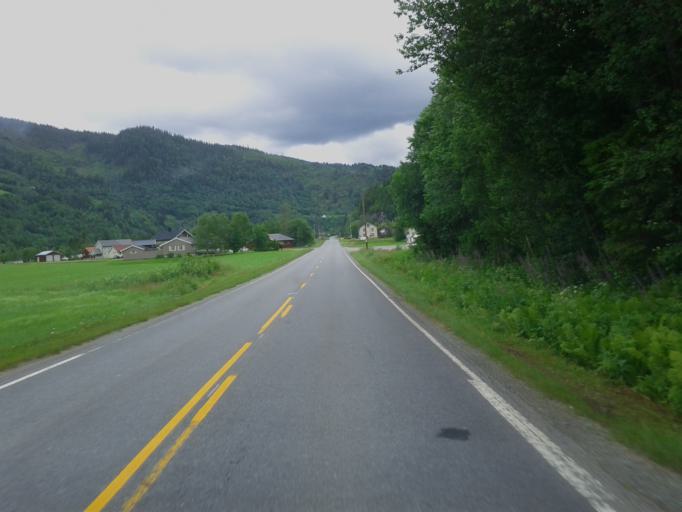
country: NO
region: Sor-Trondelag
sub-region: Midtre Gauldal
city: Storen
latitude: 62.9506
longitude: 10.6076
